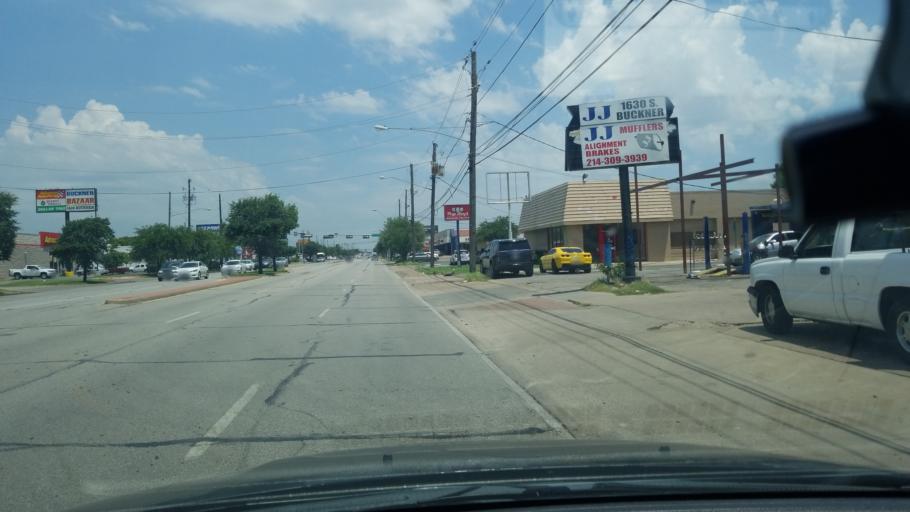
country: US
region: Texas
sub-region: Dallas County
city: Balch Springs
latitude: 32.7402
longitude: -96.6828
